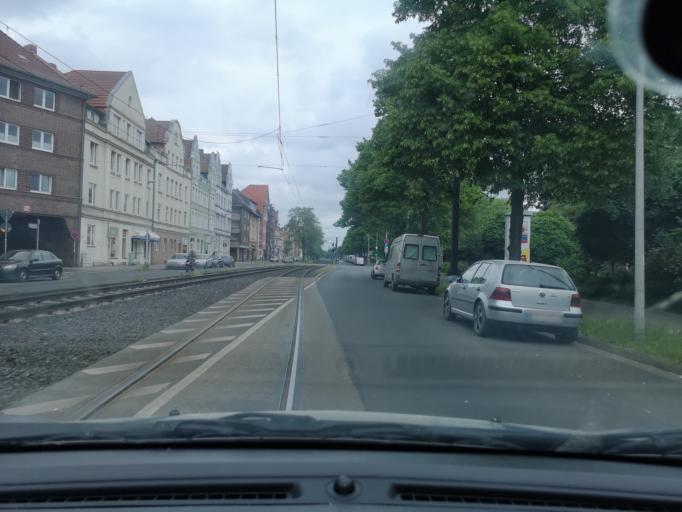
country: DE
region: Lower Saxony
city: Hannover
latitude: 52.3978
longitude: 9.6740
